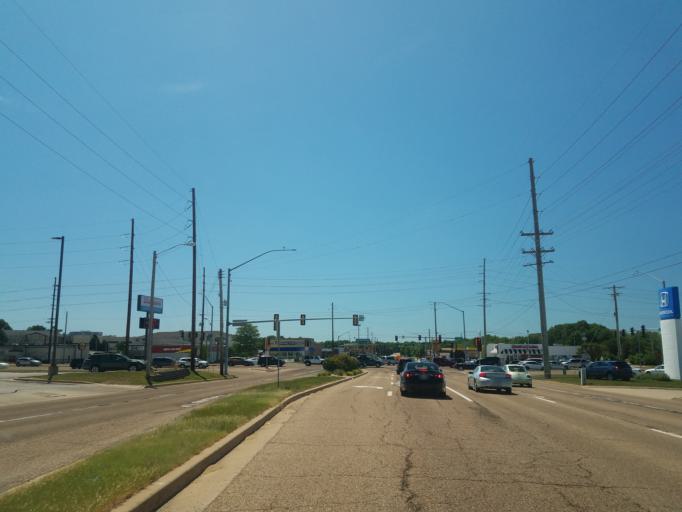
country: US
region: Illinois
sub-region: McLean County
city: Normal
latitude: 40.5027
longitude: -88.9520
